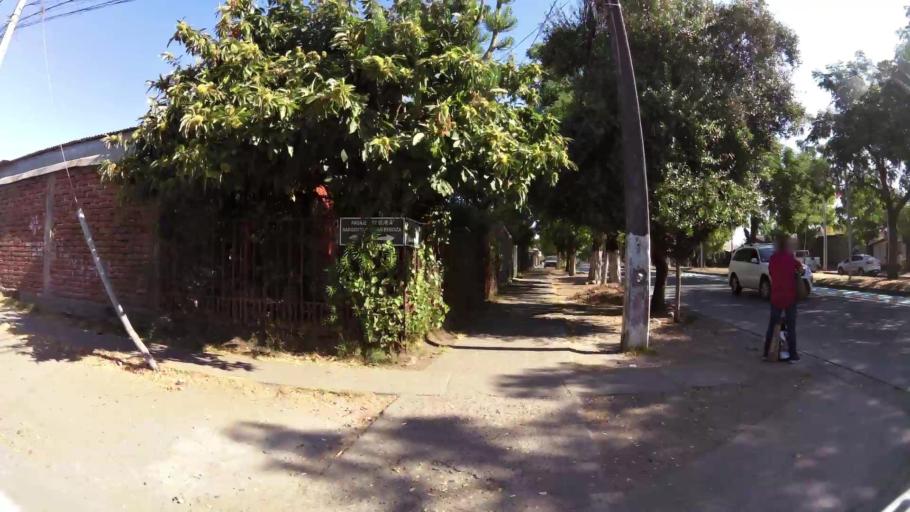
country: CL
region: Maule
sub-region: Provincia de Talca
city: Talca
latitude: -35.4412
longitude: -71.6524
